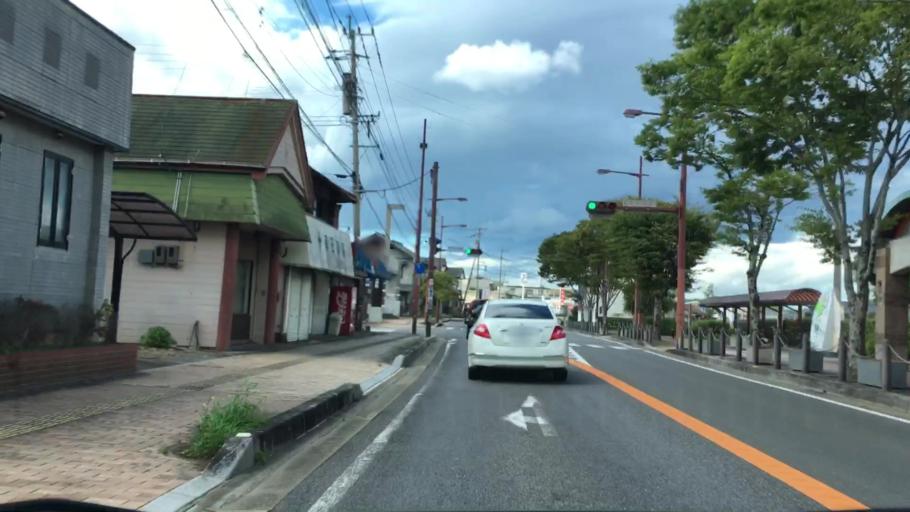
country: JP
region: Saga Prefecture
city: Imaricho-ko
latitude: 33.2100
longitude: 129.8498
